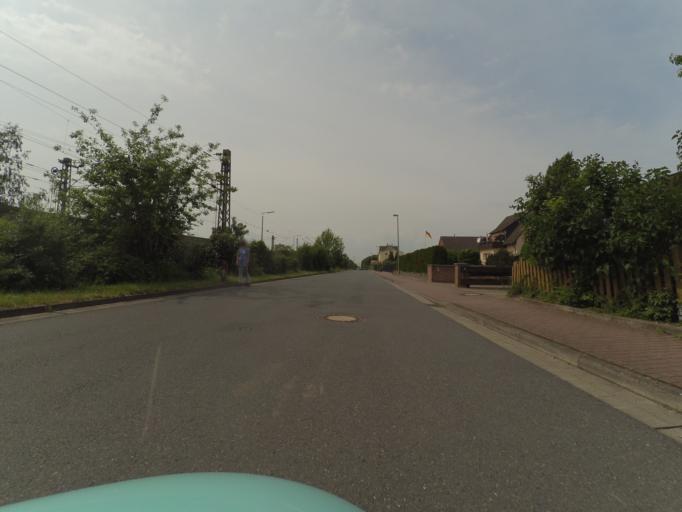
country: DE
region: Lower Saxony
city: Arpke
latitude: 52.3543
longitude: 10.1163
